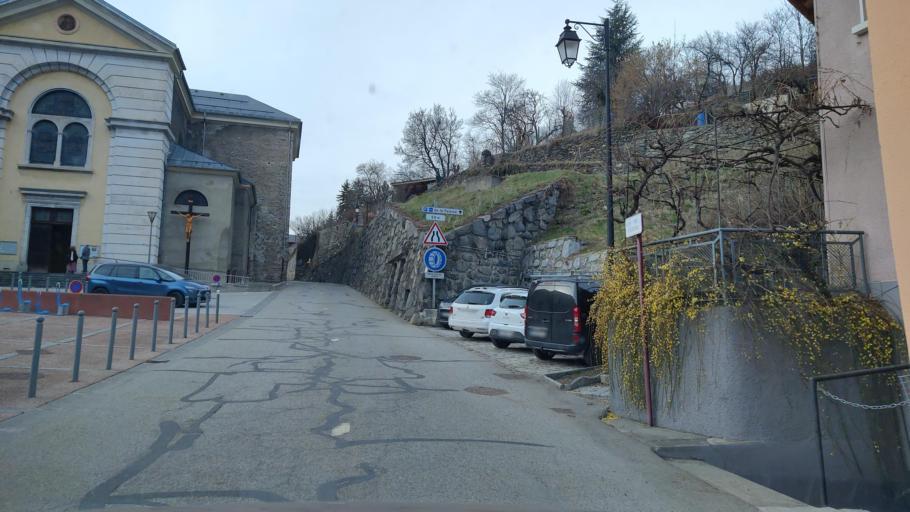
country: FR
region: Rhone-Alpes
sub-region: Departement de la Savoie
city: Saint-Michel-de-Maurienne
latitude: 45.2191
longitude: 6.4736
